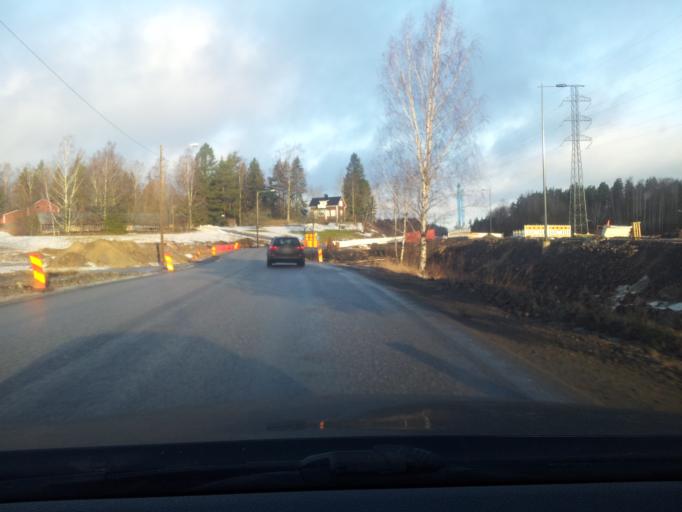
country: FI
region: Uusimaa
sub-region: Helsinki
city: Espoo
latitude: 60.1714
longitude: 24.6164
